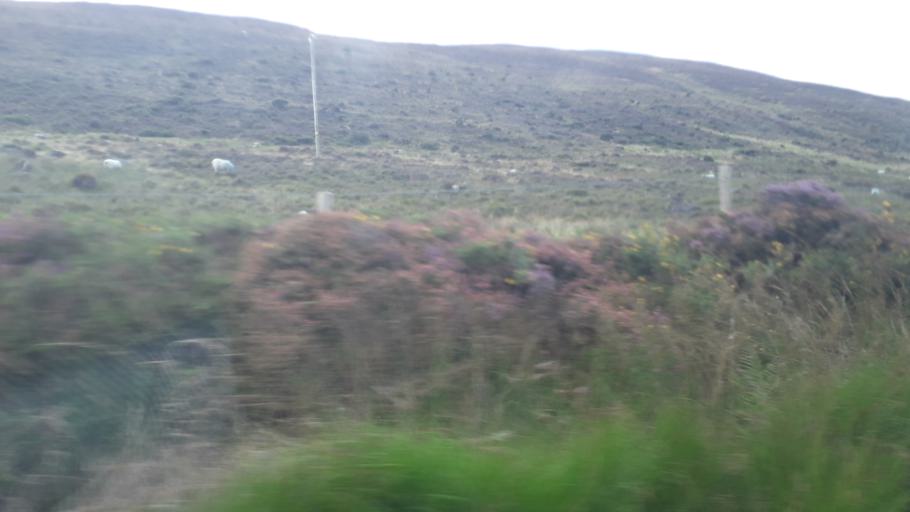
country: GB
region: Northern Ireland
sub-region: Down District
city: Warrenpoint
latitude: 54.0541
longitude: -6.2719
